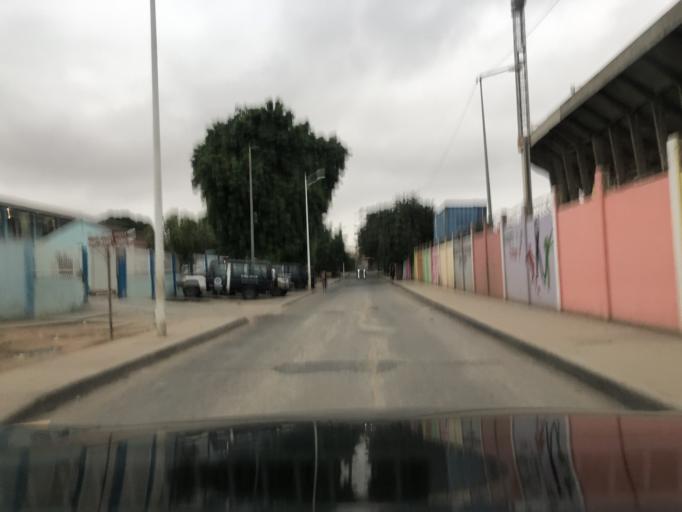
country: AO
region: Luanda
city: Luanda
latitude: -8.8276
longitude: 13.2569
